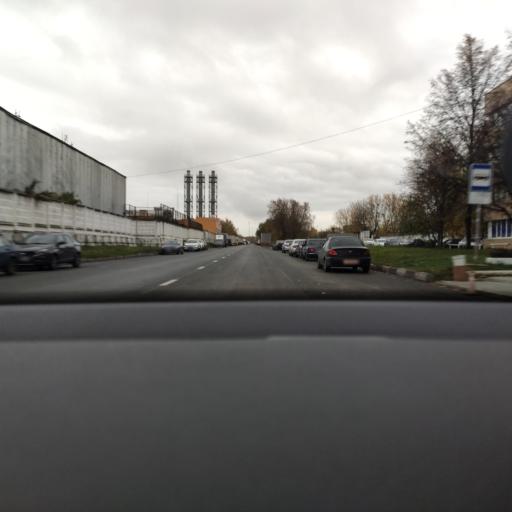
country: RU
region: Moscow
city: Mikhalkovo
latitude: 55.6759
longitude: 37.4288
